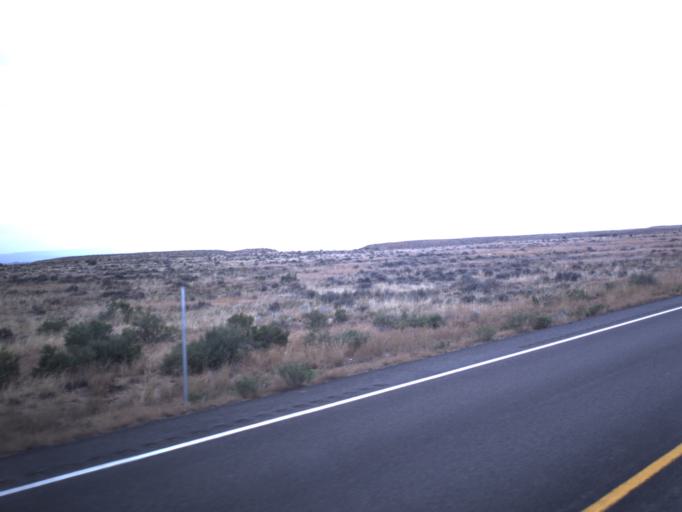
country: US
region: Utah
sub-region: Uintah County
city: Naples
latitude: 40.2833
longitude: -109.4697
